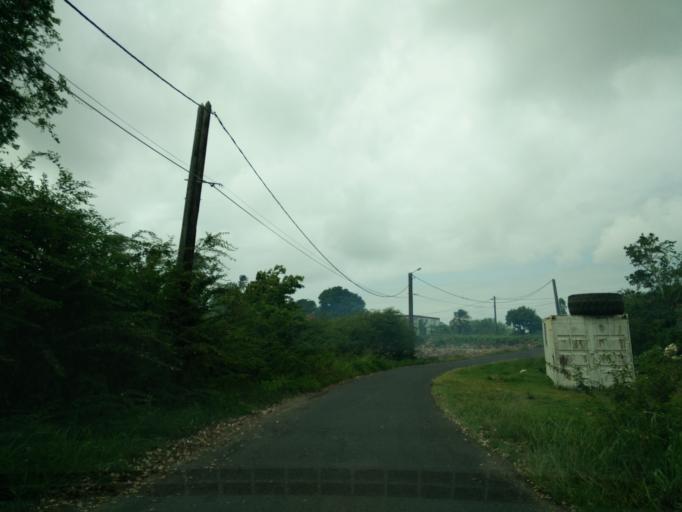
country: GP
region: Guadeloupe
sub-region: Guadeloupe
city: Grand-Bourg
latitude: 15.9083
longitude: -61.2764
